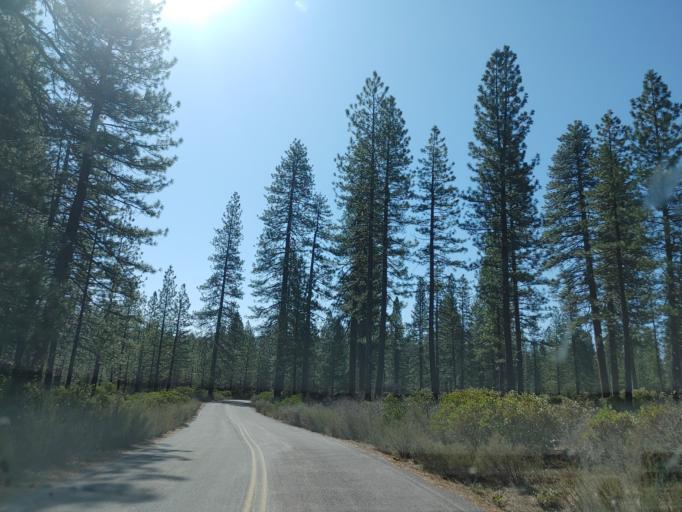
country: US
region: California
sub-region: Siskiyou County
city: McCloud
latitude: 41.2505
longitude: -122.0276
